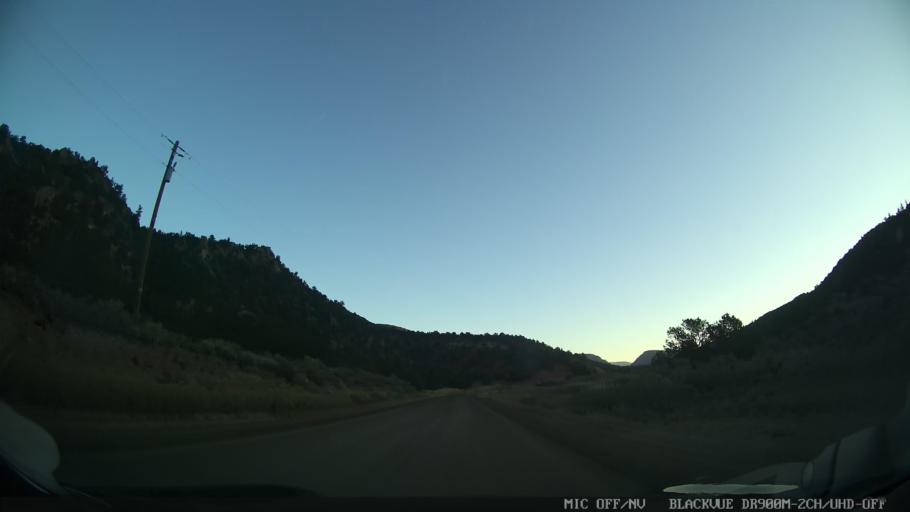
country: US
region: Colorado
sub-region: Eagle County
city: Edwards
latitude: 39.8765
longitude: -106.6339
